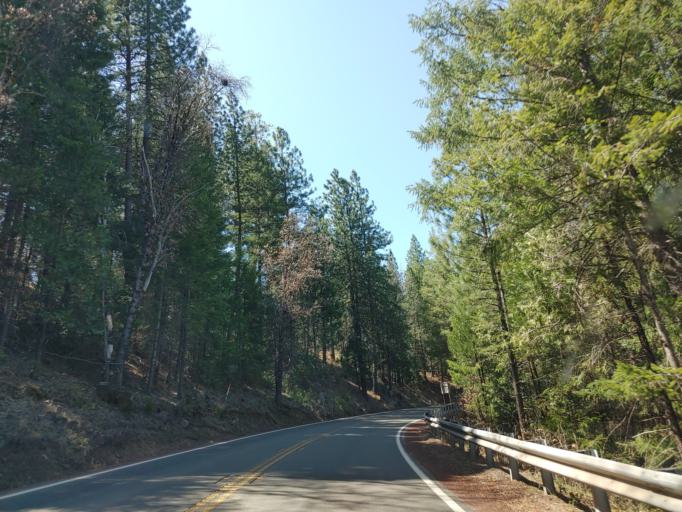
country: US
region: California
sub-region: Shasta County
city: Burney
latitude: 41.0150
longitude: -121.6280
